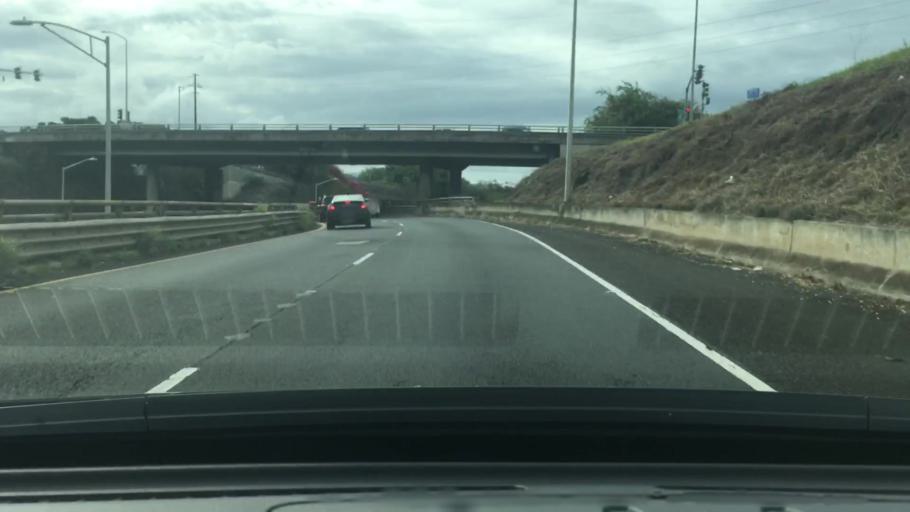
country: US
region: Hawaii
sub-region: Honolulu County
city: Honolulu
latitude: 21.3374
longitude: -157.8832
